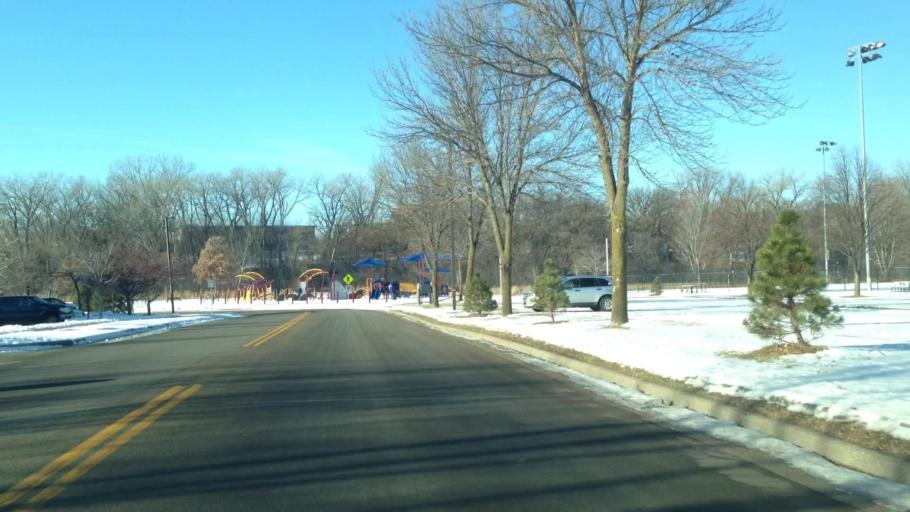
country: US
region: Minnesota
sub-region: Hennepin County
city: Golden Valley
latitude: 44.9858
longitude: -93.3413
